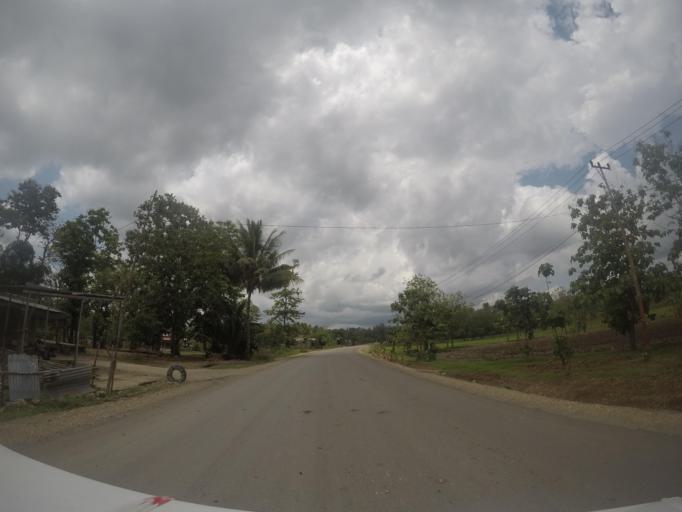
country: TL
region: Baucau
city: Baucau
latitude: -8.5374
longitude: 126.4192
